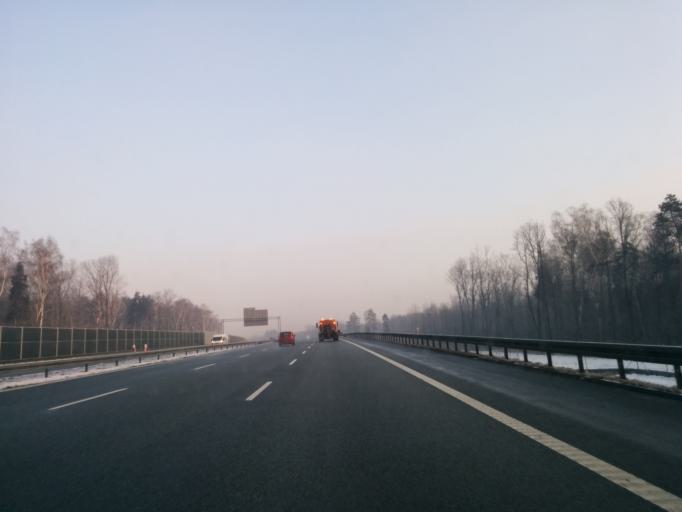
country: PL
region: Silesian Voivodeship
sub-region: Gliwice
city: Gliwice
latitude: 50.3214
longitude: 18.7277
